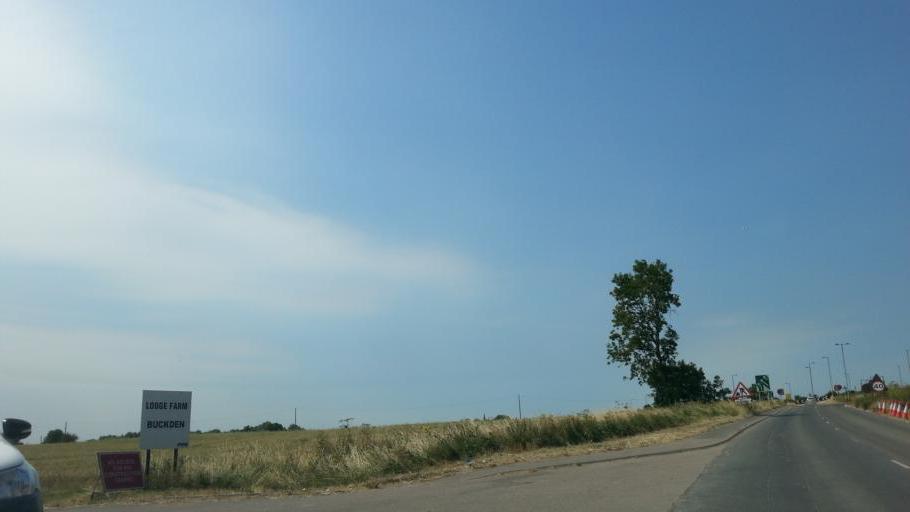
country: GB
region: England
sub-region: Cambridgeshire
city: Buckden
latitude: 52.3037
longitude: -0.2426
